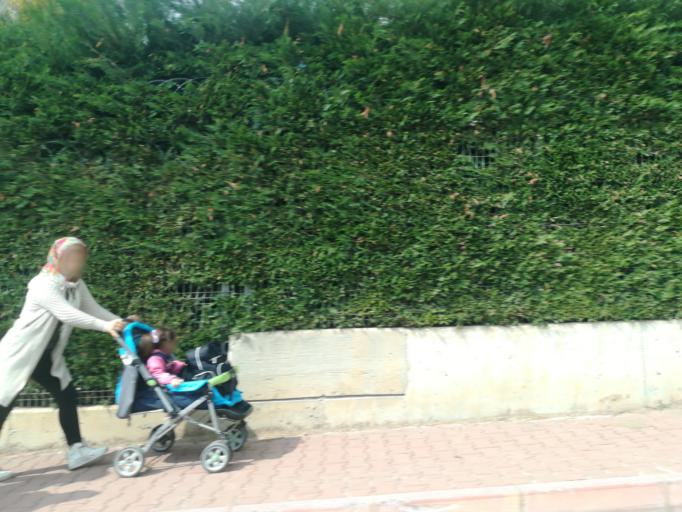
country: TR
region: Adana
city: Seyhan
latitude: 37.0254
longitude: 35.2735
